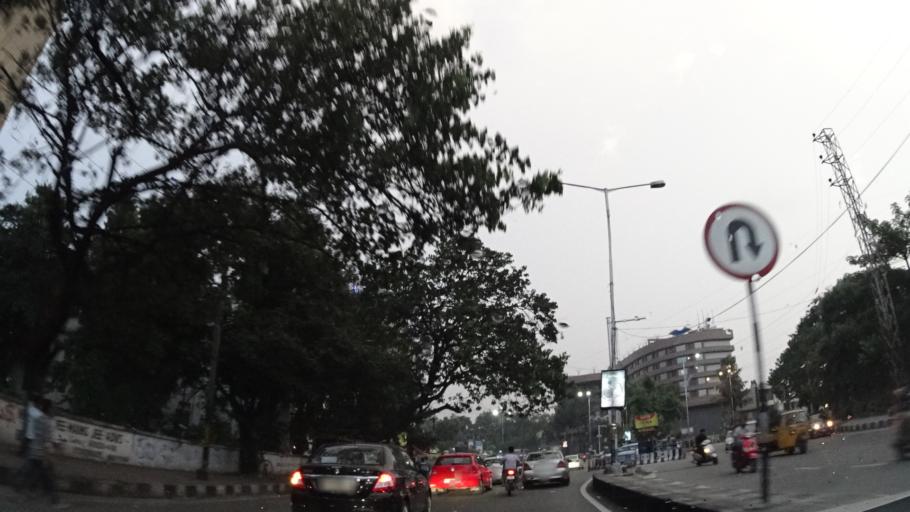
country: IN
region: Telangana
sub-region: Hyderabad
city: Hyderabad
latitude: 17.4206
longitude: 78.4485
